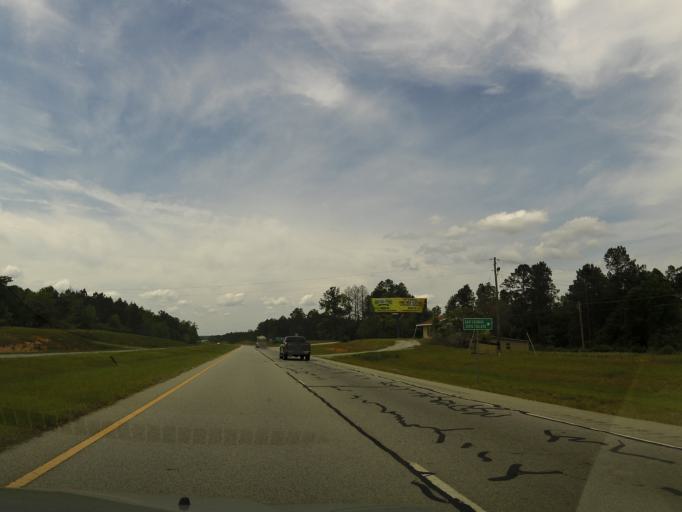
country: US
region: Georgia
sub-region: Emanuel County
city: Swainsboro
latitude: 32.5397
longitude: -82.3123
